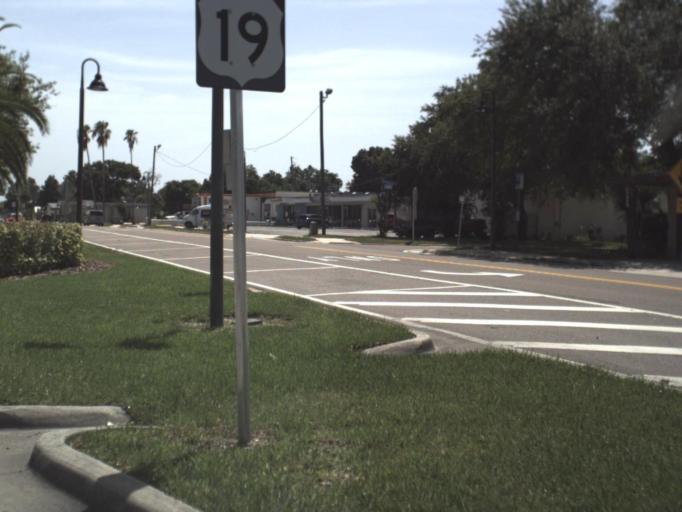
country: US
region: Florida
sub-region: Pinellas County
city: Clearwater
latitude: 27.9836
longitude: -82.7960
